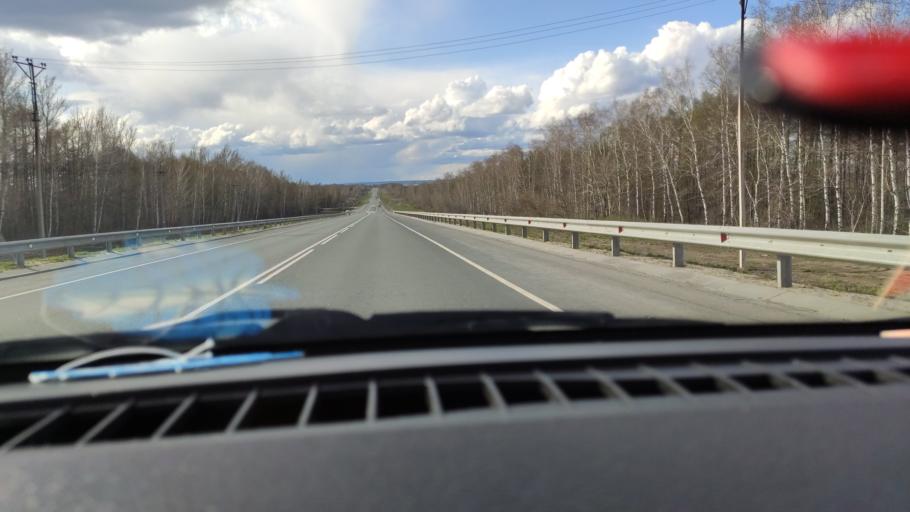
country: RU
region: Saratov
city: Shikhany
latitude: 52.1514
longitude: 47.1875
